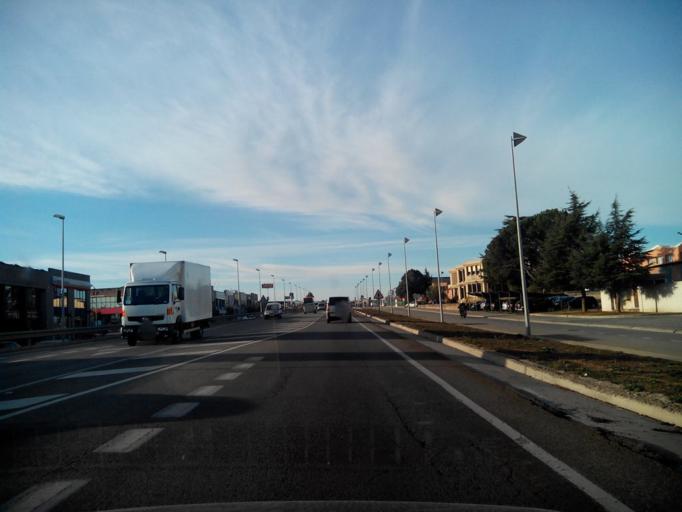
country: ES
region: Catalonia
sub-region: Provincia de Barcelona
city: Sant Fruitos de Bages
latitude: 41.7497
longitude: 1.8619
